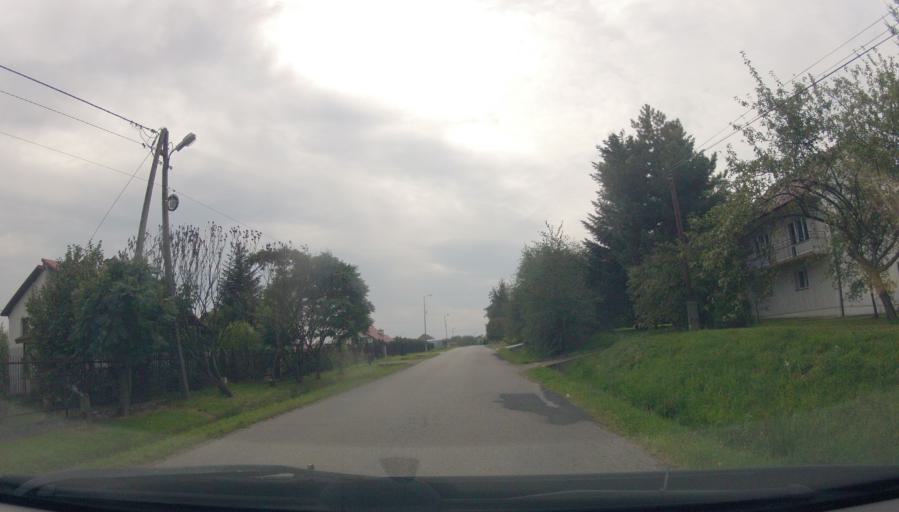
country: PL
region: Lesser Poland Voivodeship
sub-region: Powiat wielicki
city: Pawlikowice
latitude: 49.9522
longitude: 20.0209
